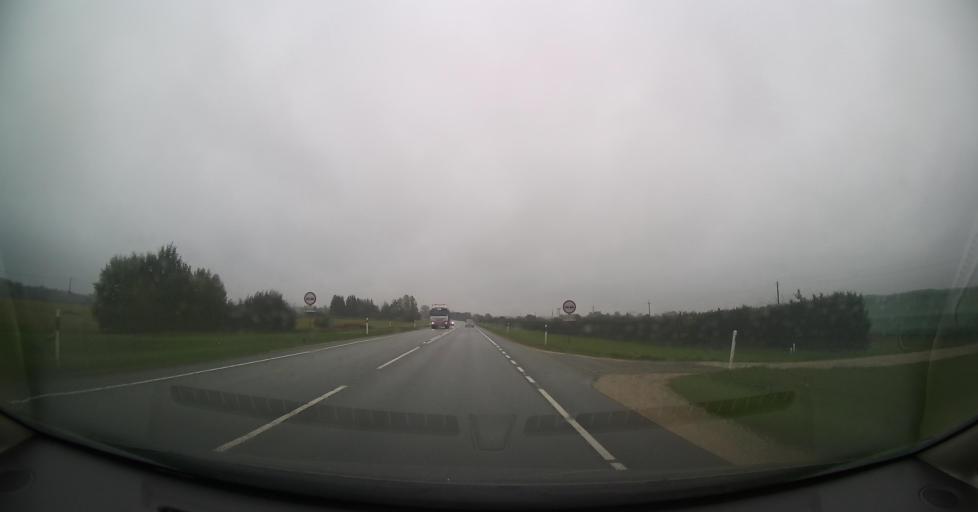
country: EE
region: Jaervamaa
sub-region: Paide linn
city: Paide
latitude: 58.8906
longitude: 25.6687
